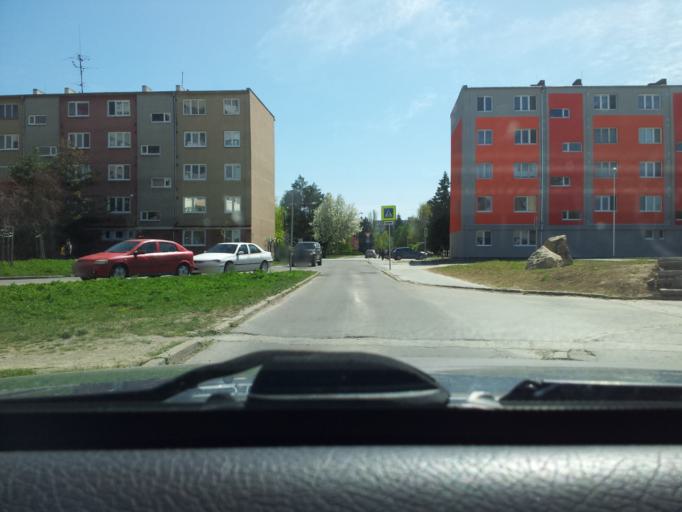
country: SK
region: Nitriansky
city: Levice
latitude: 48.2157
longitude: 18.6007
